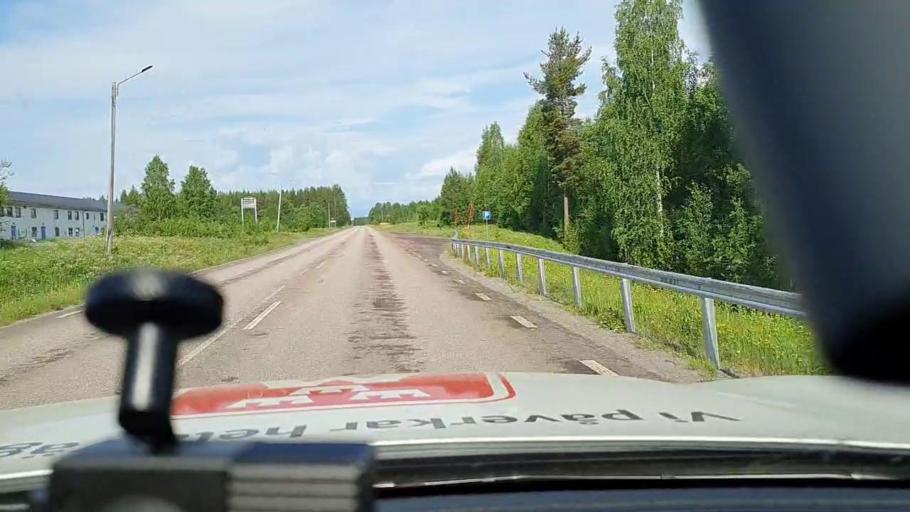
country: SE
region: Norrbotten
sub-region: Alvsbyns Kommun
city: AElvsbyn
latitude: 66.0159
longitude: 21.1582
